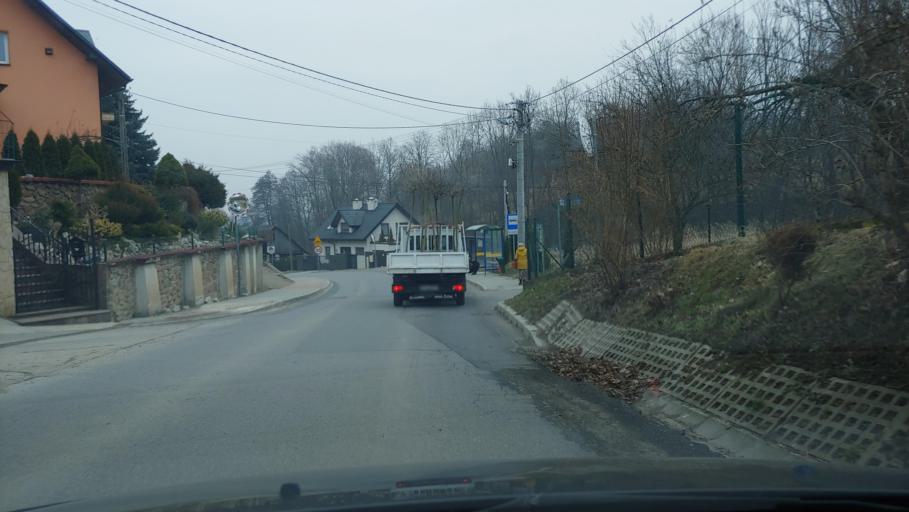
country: PL
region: Lesser Poland Voivodeship
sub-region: Powiat krakowski
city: Balice
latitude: 50.0908
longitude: 19.7823
